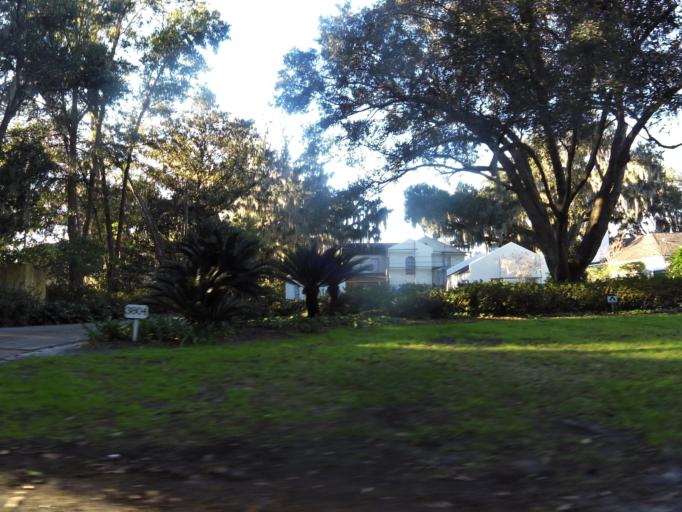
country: US
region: Florida
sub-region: Duval County
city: Jacksonville
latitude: 30.2800
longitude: -81.7011
